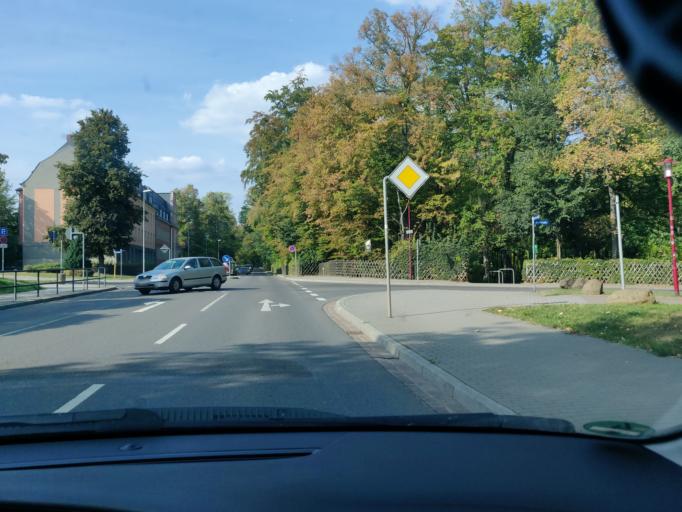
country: DE
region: Saxony
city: Mittweida
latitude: 50.9867
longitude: 12.9680
